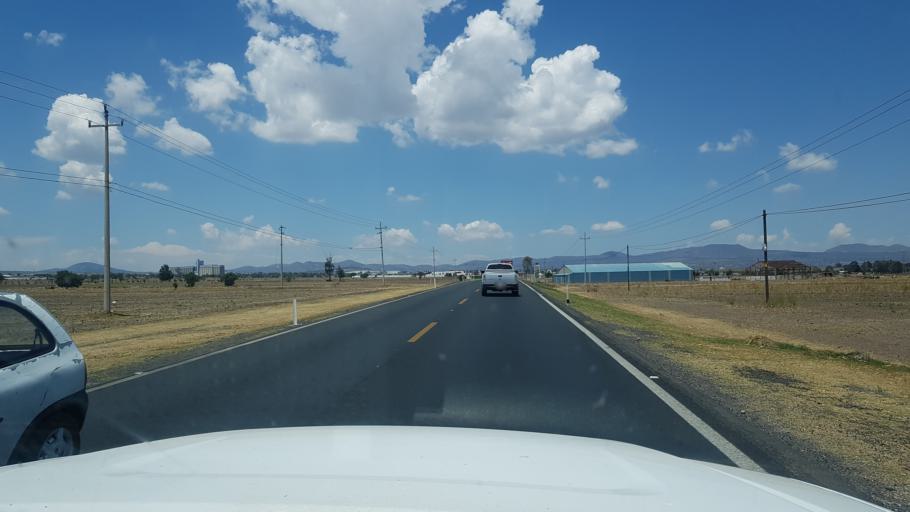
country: MX
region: Hidalgo
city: Calpulalpan
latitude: 19.5789
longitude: -98.5242
